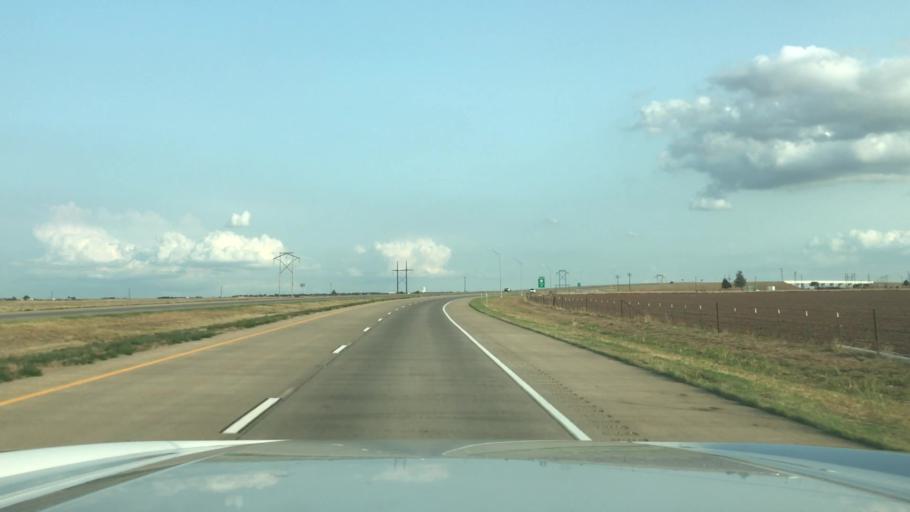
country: US
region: Texas
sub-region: Swisher County
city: Tulia
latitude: 34.5845
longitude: -101.7963
